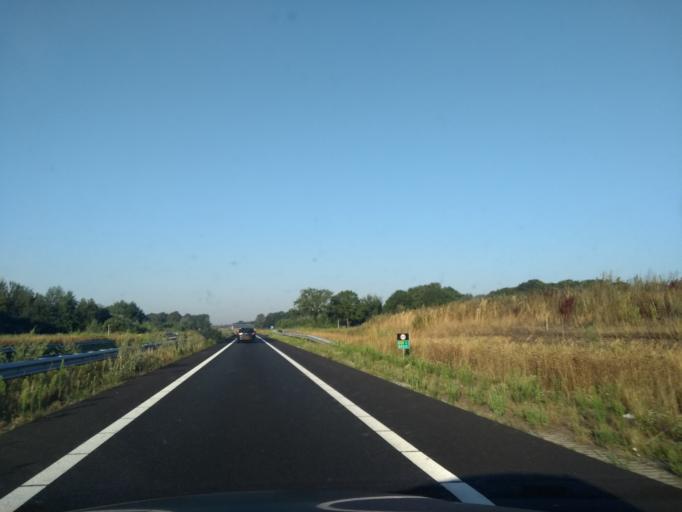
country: NL
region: Gelderland
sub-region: Berkelland
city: Eibergen
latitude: 52.1227
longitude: 6.6442
